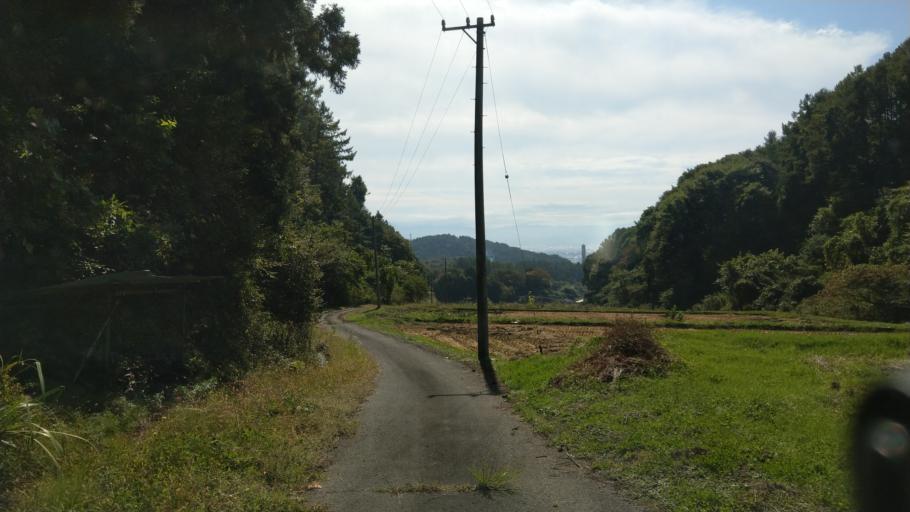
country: JP
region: Nagano
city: Komoro
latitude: 36.3596
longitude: 138.4353
